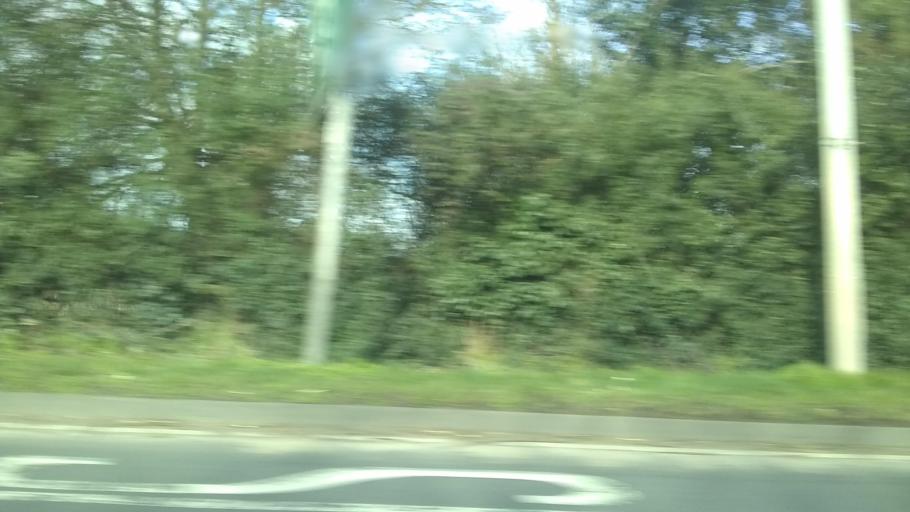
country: GB
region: England
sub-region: Worcestershire
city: Bewdley
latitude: 52.3691
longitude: -2.3428
